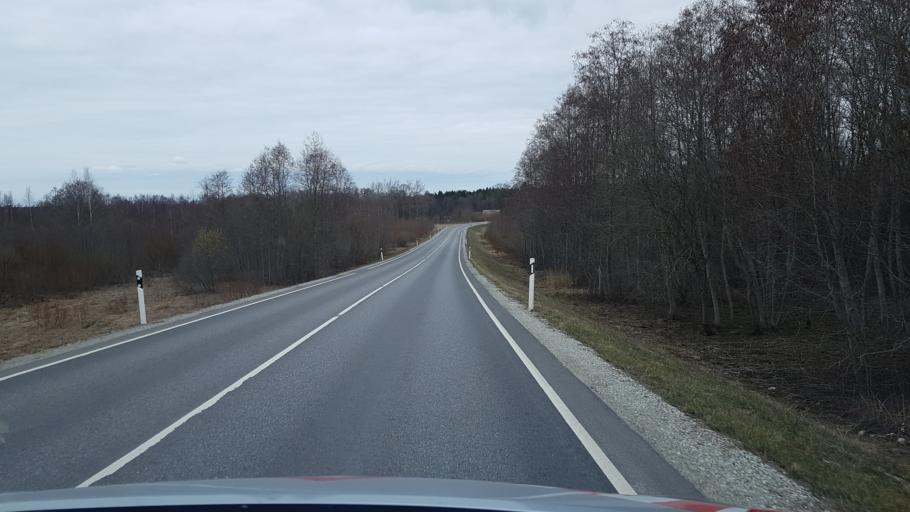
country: EE
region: Ida-Virumaa
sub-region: Narva-Joesuu linn
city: Narva-Joesuu
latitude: 59.4080
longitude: 28.0673
